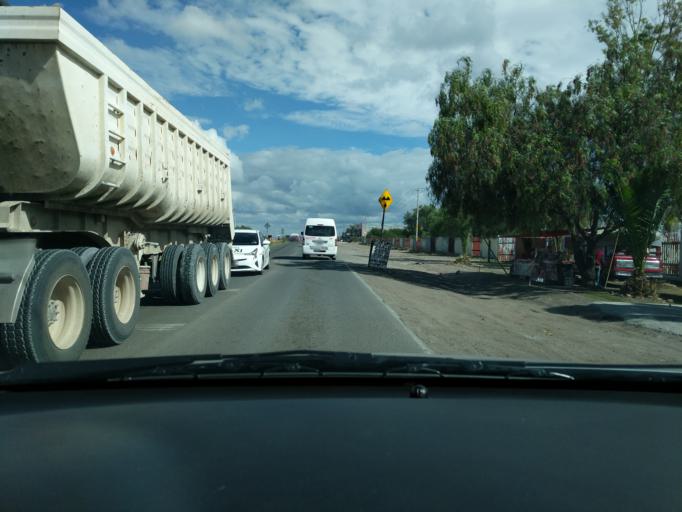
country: MX
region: Queretaro
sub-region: El Marques
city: Hacienda la Cruz [Fraccionamiento]
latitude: 20.6191
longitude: -100.2604
